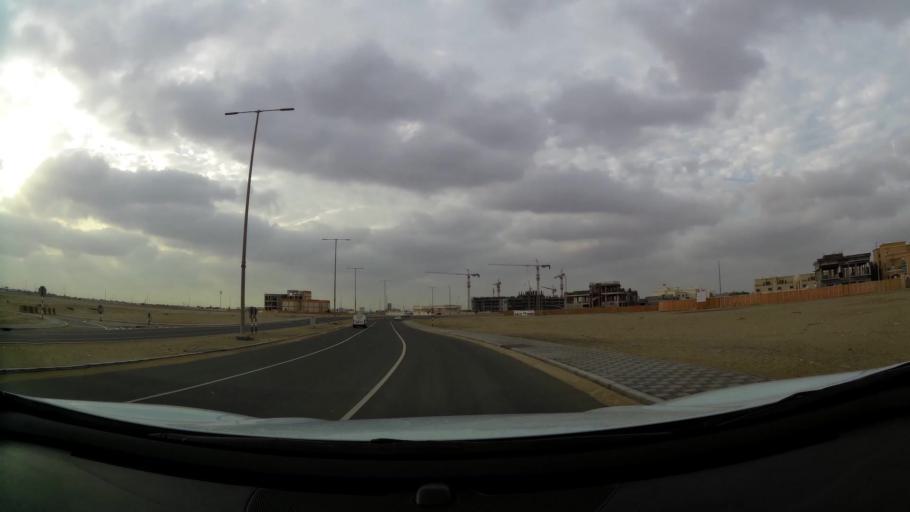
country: AE
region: Abu Dhabi
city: Abu Dhabi
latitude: 24.3503
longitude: 54.5421
